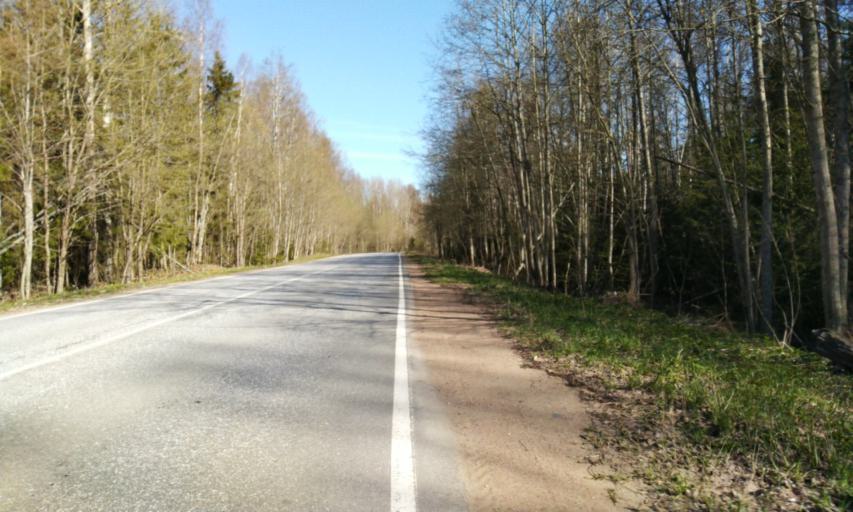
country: RU
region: Leningrad
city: Garbolovo
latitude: 60.3667
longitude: 30.4414
